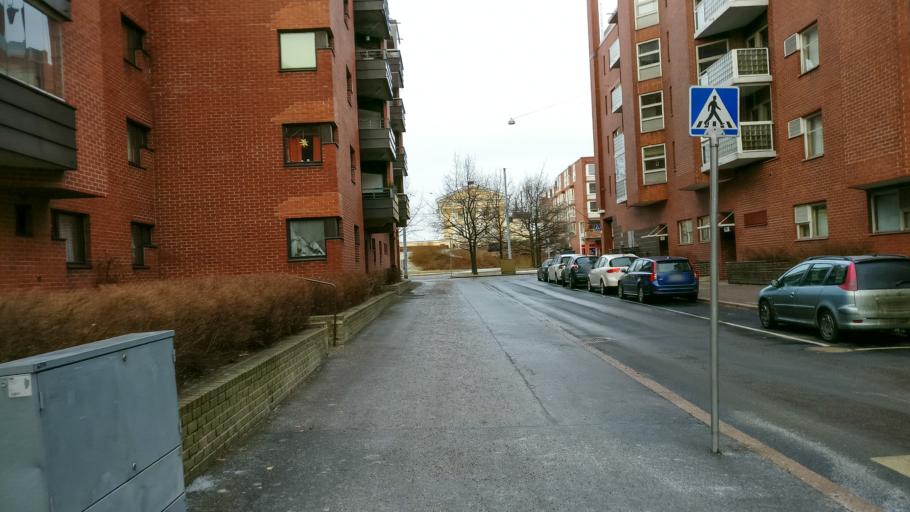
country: FI
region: Uusimaa
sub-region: Helsinki
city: Helsinki
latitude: 60.1669
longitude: 24.9752
